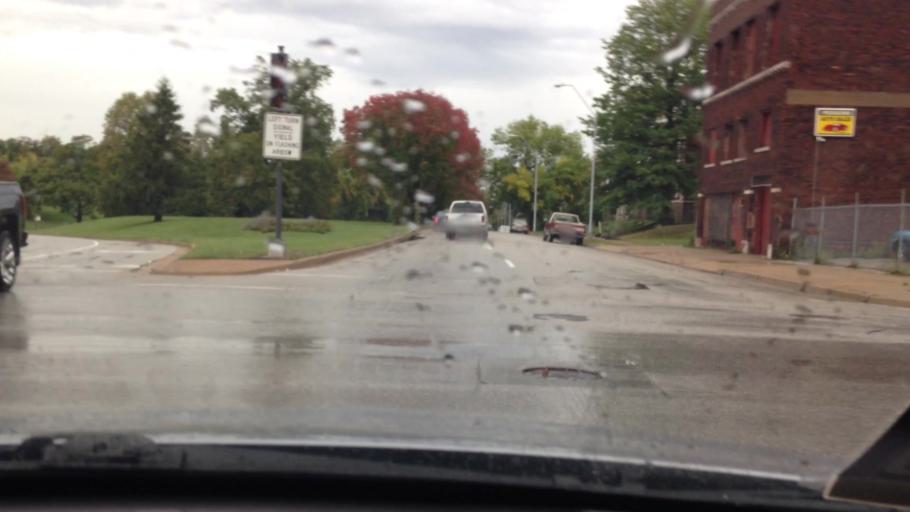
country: US
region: Missouri
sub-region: Jackson County
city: Kansas City
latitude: 39.0703
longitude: -94.5667
